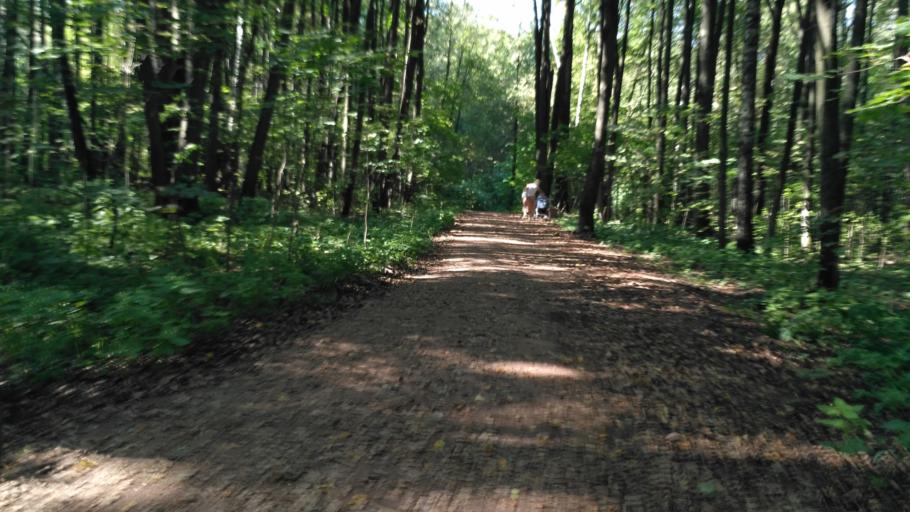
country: RU
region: Moskovskaya
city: Izmaylovo
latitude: 55.7839
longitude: 37.7718
